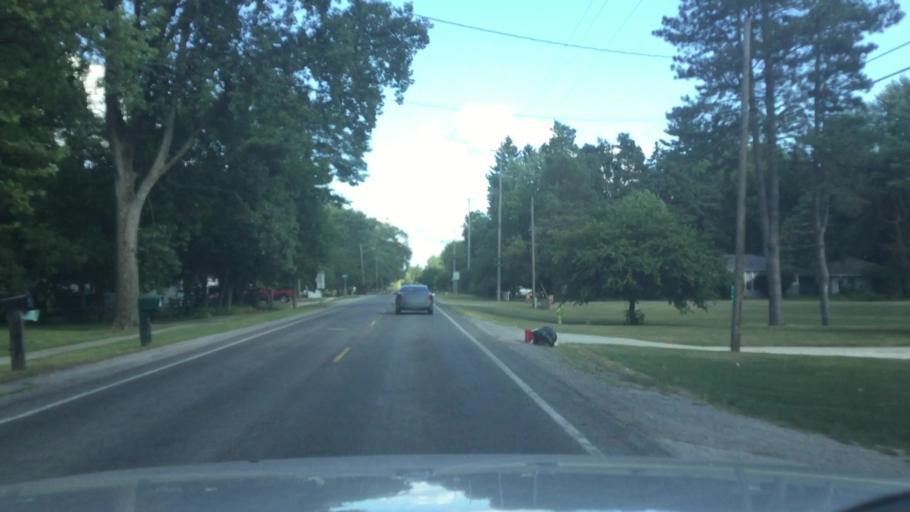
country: US
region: Michigan
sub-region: Saginaw County
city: Bridgeport
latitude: 43.3688
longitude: -83.9000
